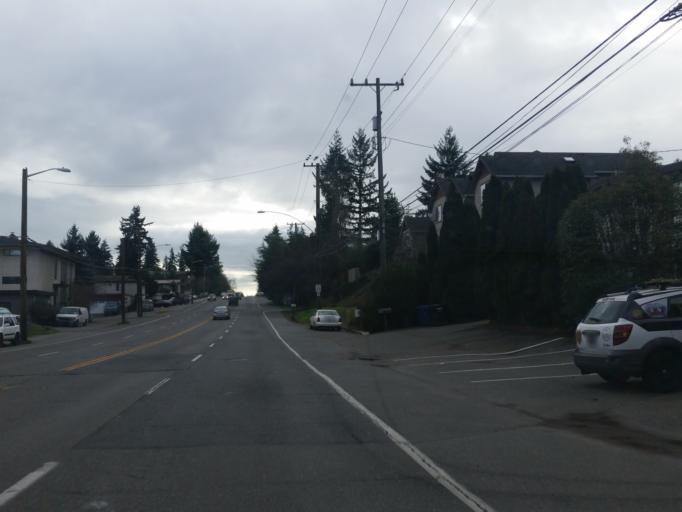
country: US
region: Washington
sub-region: King County
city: Shoreline
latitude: 47.7297
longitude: -122.3556
